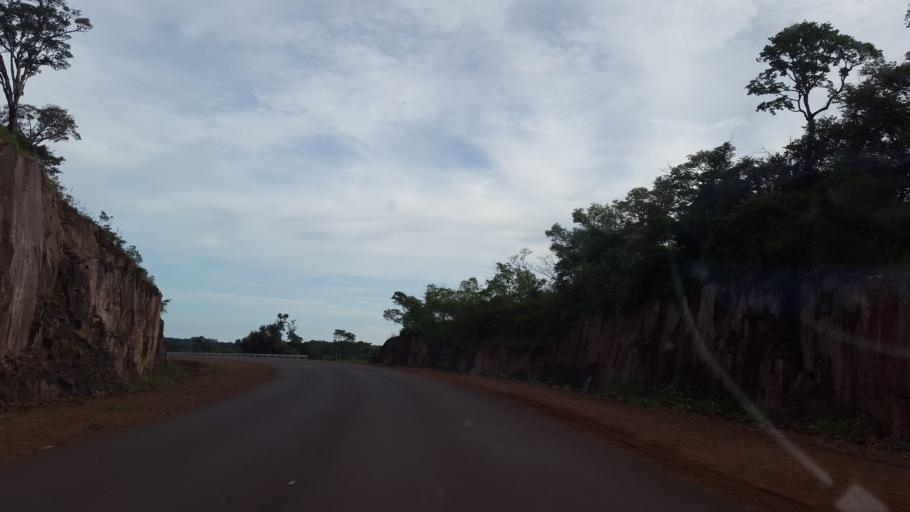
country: AR
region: Misiones
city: Bernardo de Irigoyen
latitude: -26.4511
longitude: -53.8558
